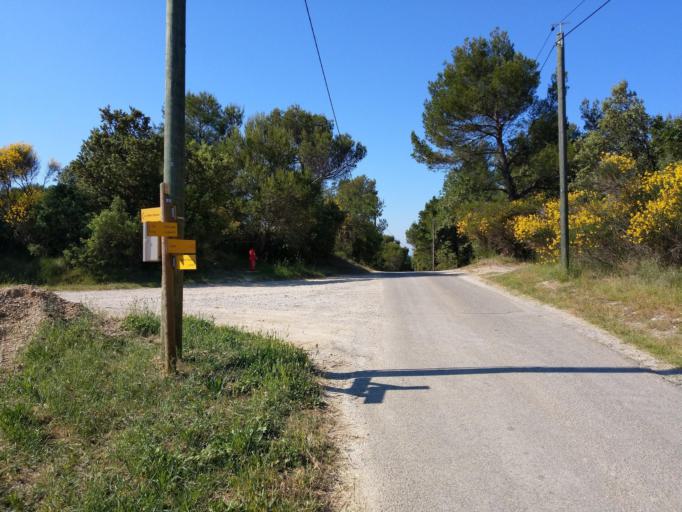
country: FR
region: Provence-Alpes-Cote d'Azur
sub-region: Departement du Vaucluse
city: Ansouis
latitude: 43.7826
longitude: 5.5089
